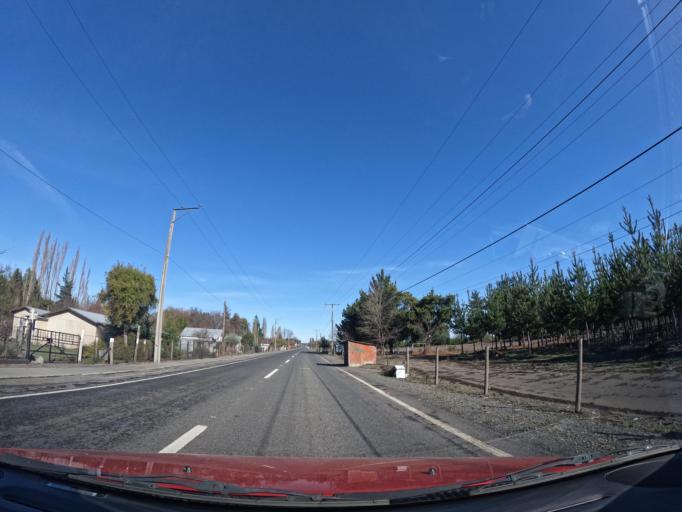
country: CL
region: Biobio
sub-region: Provincia de Biobio
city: Los Angeles
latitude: -37.3770
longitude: -72.0011
